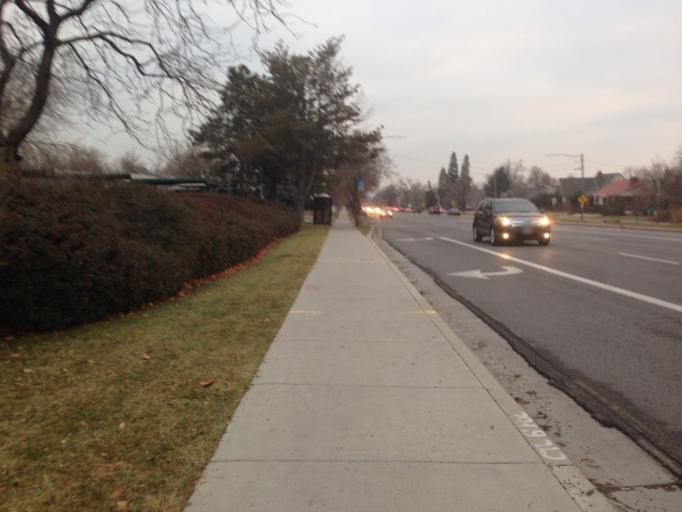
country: US
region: Utah
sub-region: Salt Lake County
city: Salt Lake City
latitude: 40.7583
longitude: -111.8536
